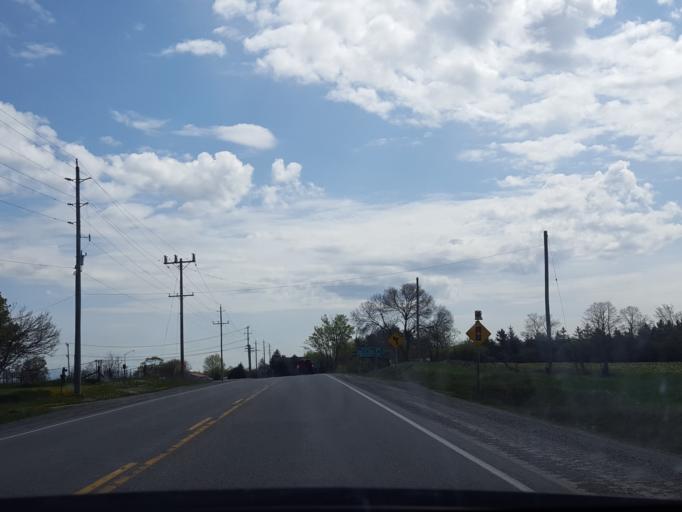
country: CA
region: Ontario
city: Oshawa
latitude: 44.1173
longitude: -78.8328
